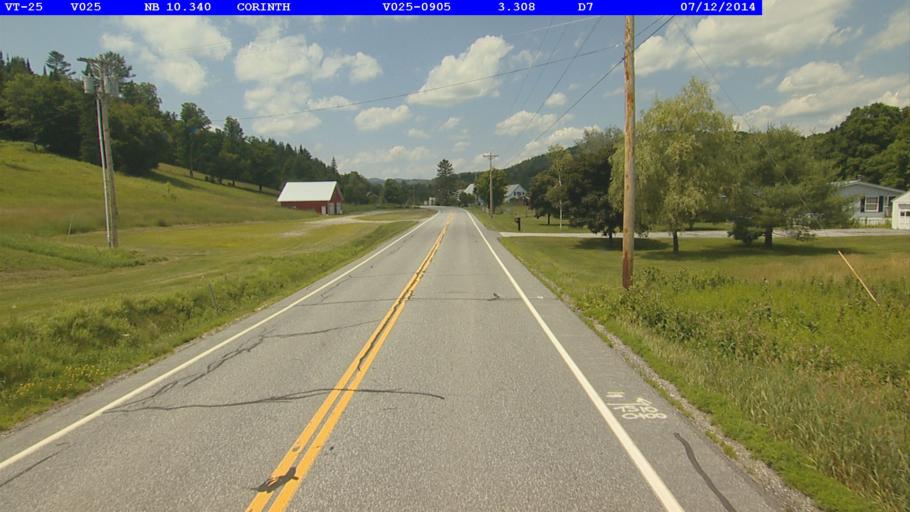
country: US
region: New Hampshire
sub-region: Grafton County
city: Haverhill
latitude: 44.0727
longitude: -72.2503
